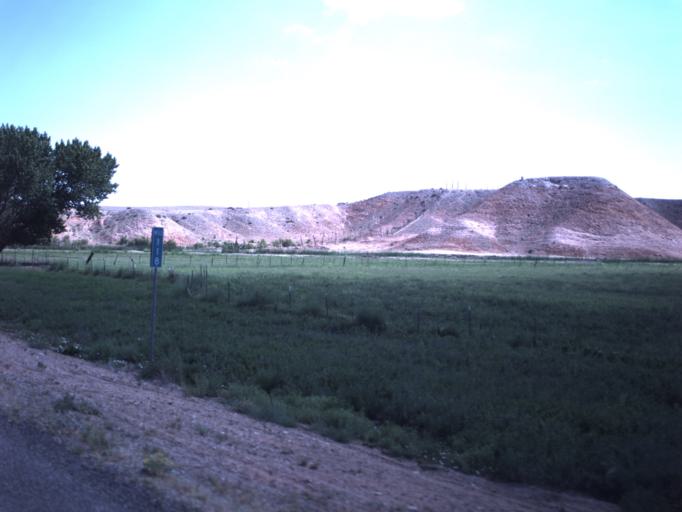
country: US
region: Utah
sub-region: Emery County
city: Ferron
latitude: 38.3922
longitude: -110.6940
